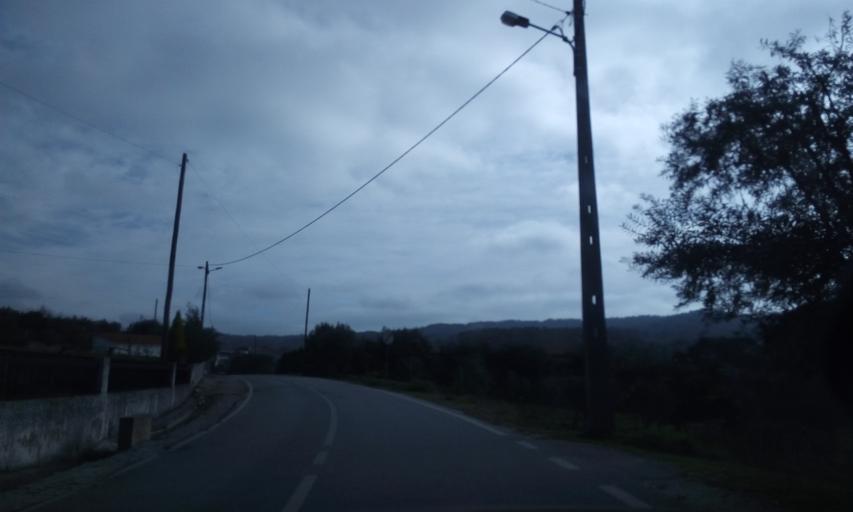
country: PT
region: Guarda
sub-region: Fornos de Algodres
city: Fornos de Algodres
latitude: 40.7036
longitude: -7.5597
